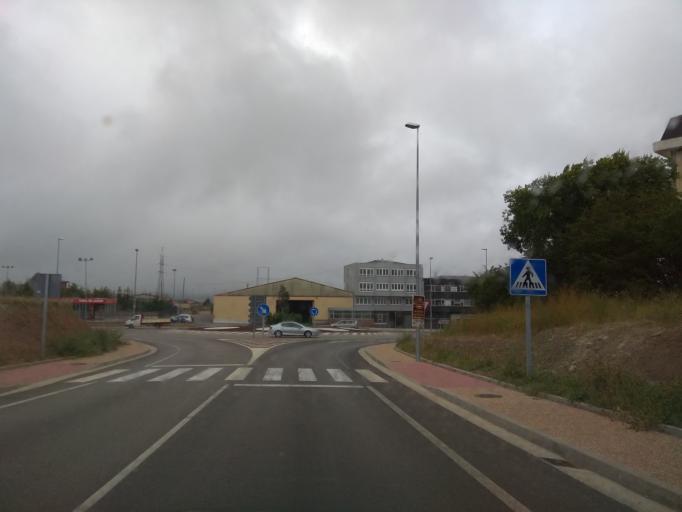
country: ES
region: Cantabria
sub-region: Provincia de Cantabria
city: Reinosa
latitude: 43.0070
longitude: -4.1299
